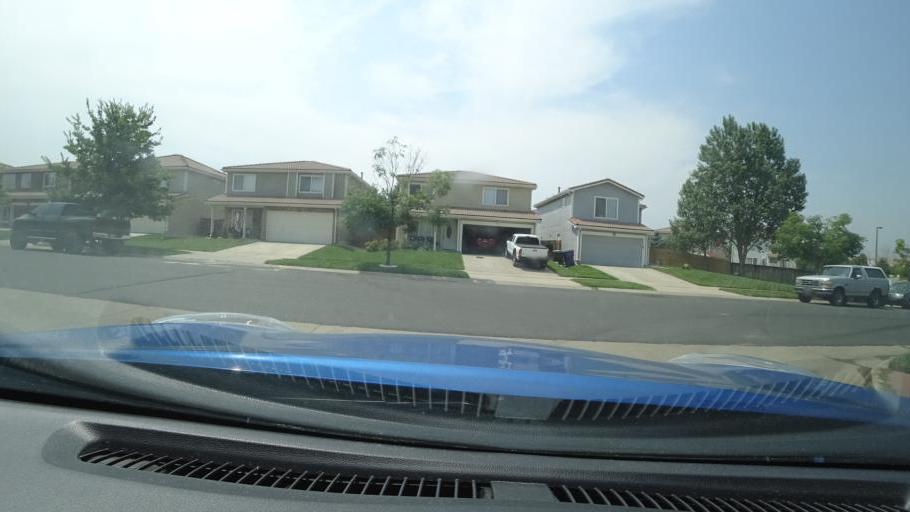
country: US
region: Colorado
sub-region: Adams County
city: Aurora
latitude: 39.7730
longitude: -104.7365
